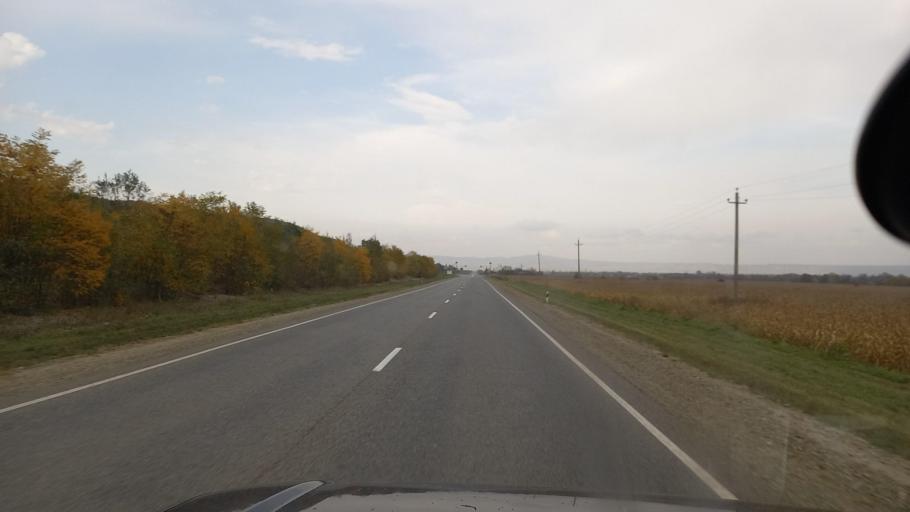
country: RU
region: Krasnodarskiy
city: Shedok
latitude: 44.2328
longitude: 40.8571
